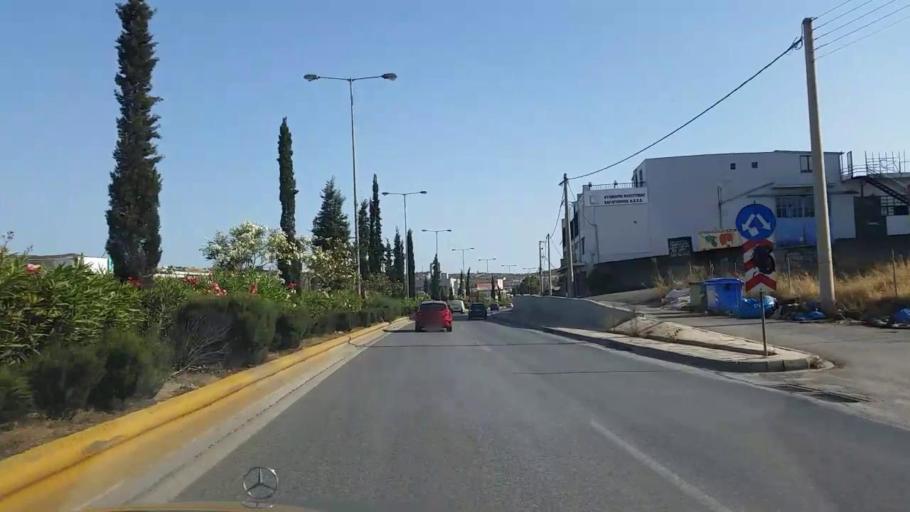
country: GR
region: Attica
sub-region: Nomarchia Anatolikis Attikis
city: Koropi
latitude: 37.8898
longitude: 23.8815
